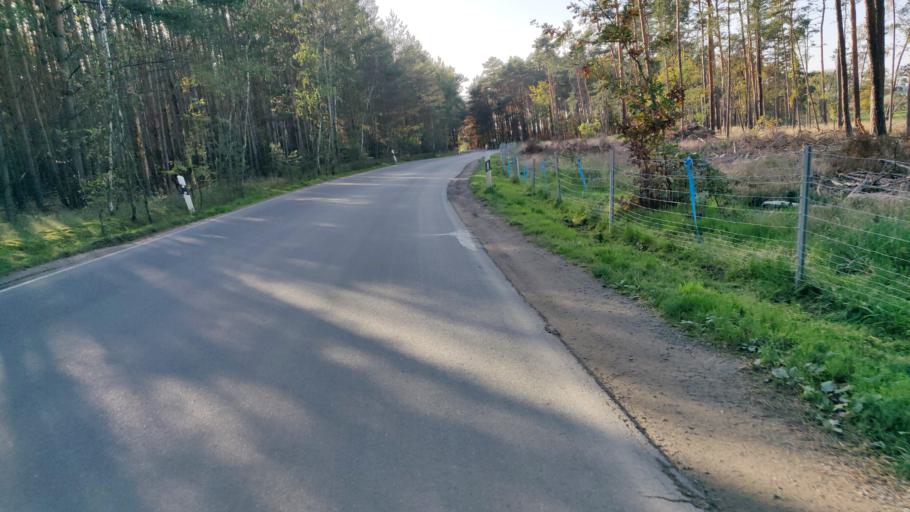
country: DE
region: Brandenburg
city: Kroppen
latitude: 51.3495
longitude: 13.8104
